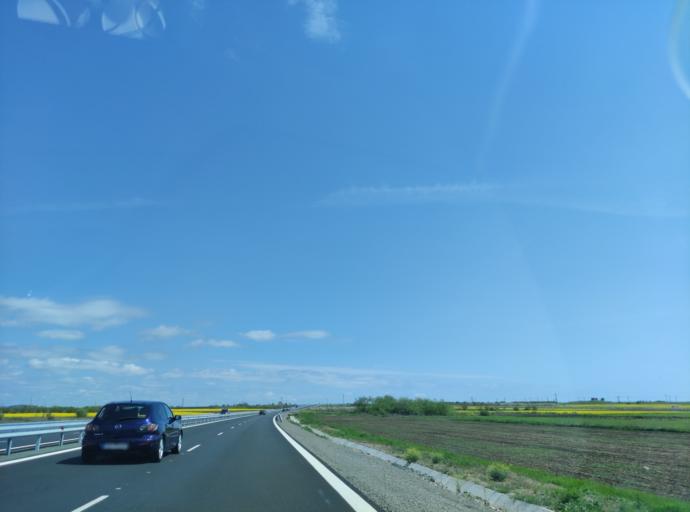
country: BG
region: Burgas
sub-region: Obshtina Pomorie
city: Pomorie
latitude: 42.5732
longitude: 27.5752
